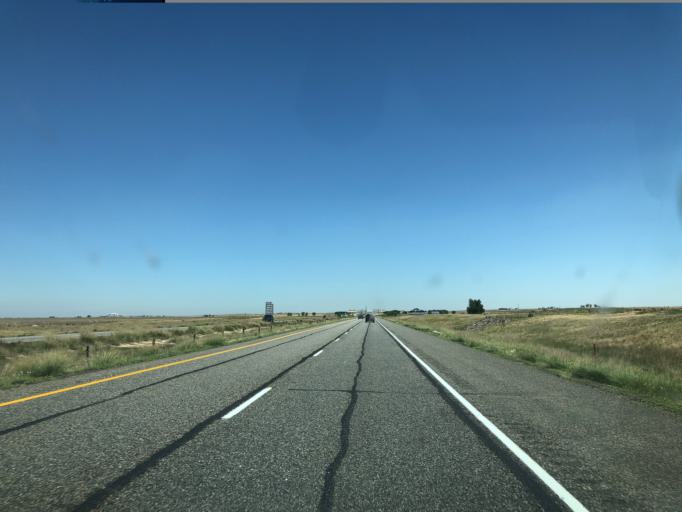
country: US
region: Colorado
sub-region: Adams County
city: Aurora
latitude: 39.7571
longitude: -104.7165
